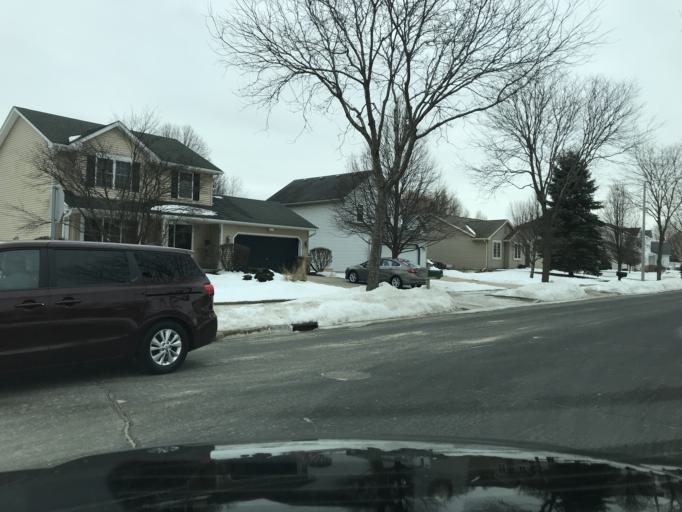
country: US
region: Wisconsin
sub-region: Dane County
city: Monona
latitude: 43.0734
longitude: -89.2851
